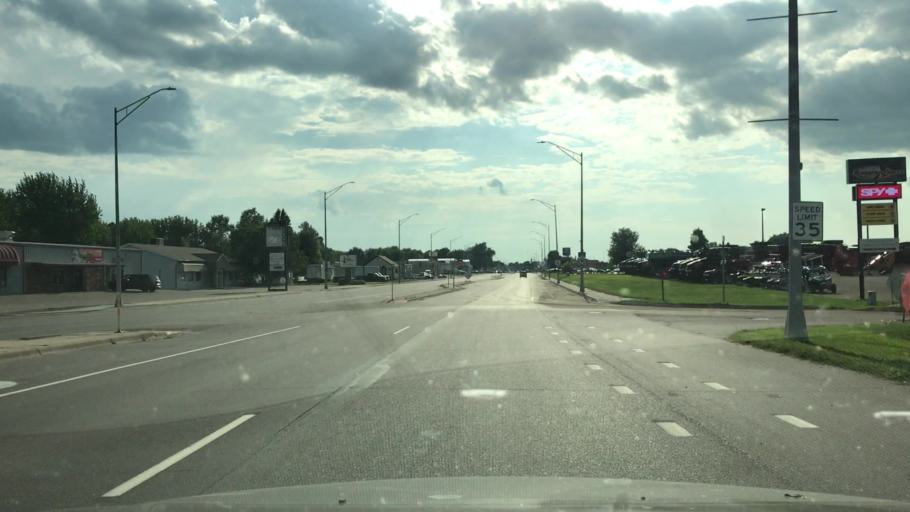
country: US
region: Minnesota
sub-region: Nobles County
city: Worthington
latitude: 43.6311
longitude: -95.5816
